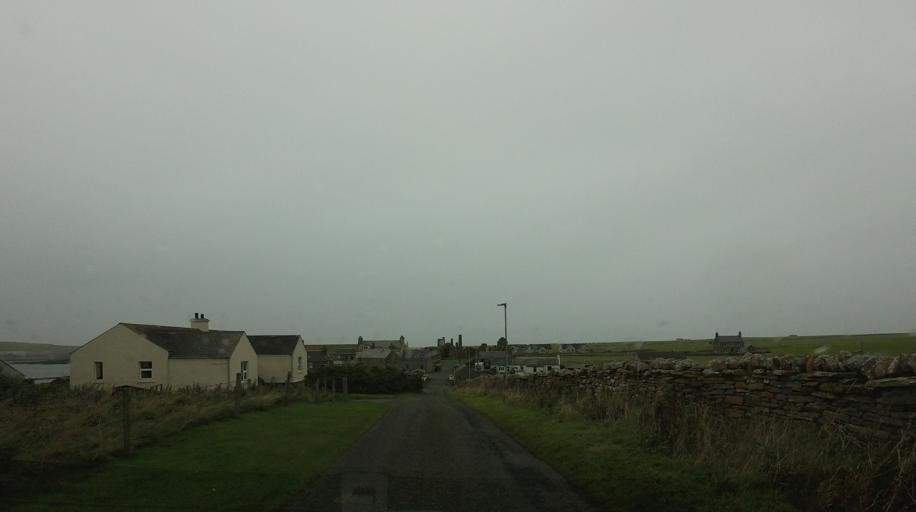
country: GB
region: Scotland
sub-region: Orkney Islands
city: Stromness
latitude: 59.1278
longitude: -3.3155
